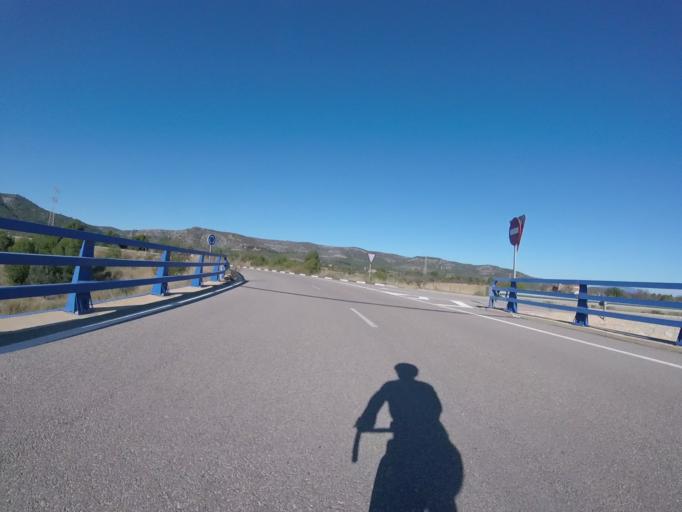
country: ES
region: Valencia
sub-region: Provincia de Castello
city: Orpesa/Oropesa del Mar
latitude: 40.1268
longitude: 0.1187
